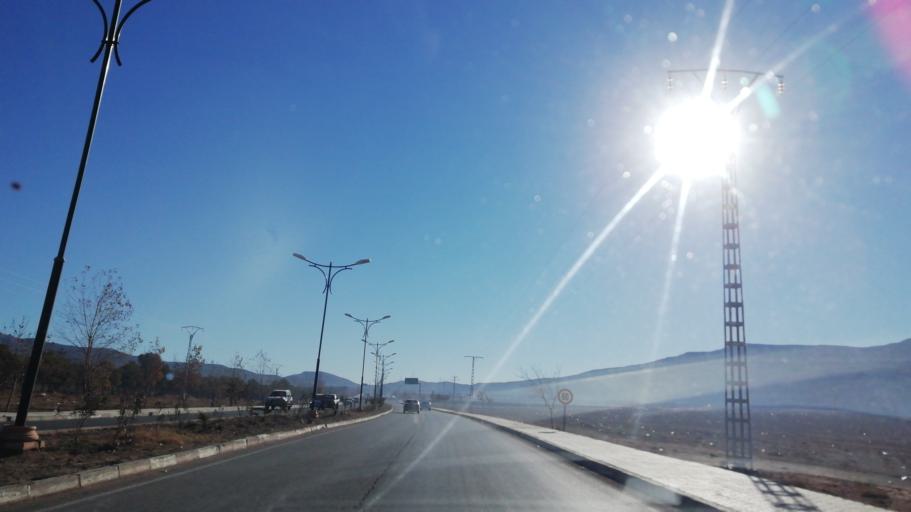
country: DZ
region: El Bayadh
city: El Bayadh
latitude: 33.6627
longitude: 1.0530
